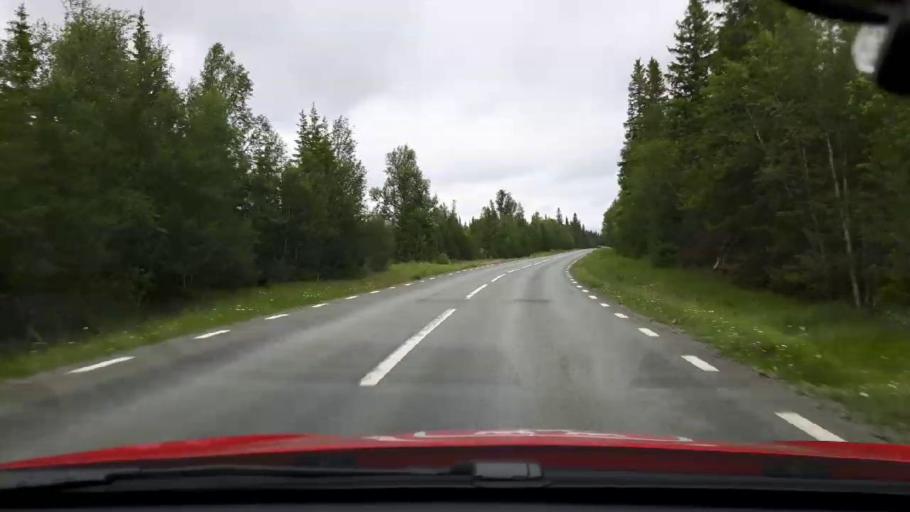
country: SE
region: Jaemtland
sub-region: Are Kommun
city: Are
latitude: 63.3421
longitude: 12.5703
